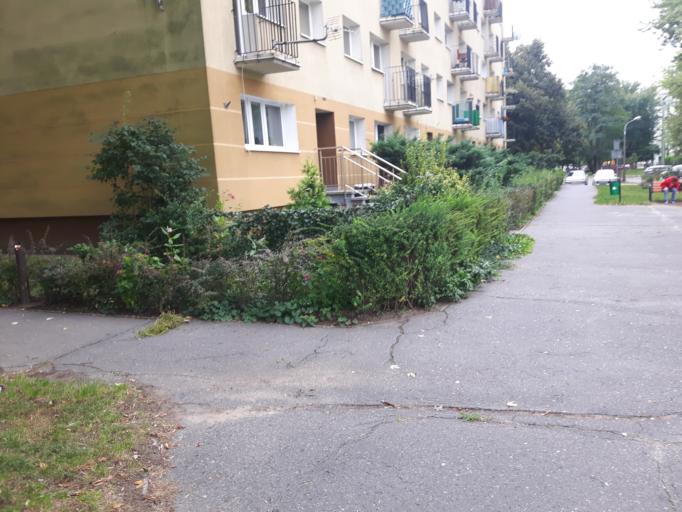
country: PL
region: Masovian Voivodeship
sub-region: Warszawa
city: Bielany
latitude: 52.2945
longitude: 20.9363
